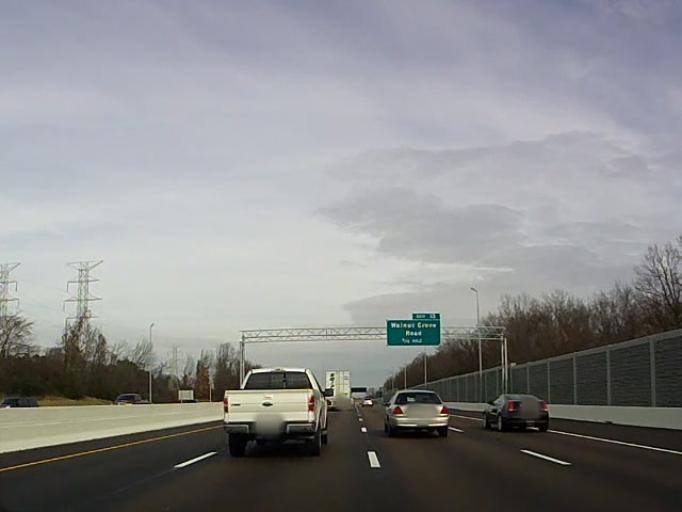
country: US
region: Tennessee
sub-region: Shelby County
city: Germantown
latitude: 35.1179
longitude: -89.8691
